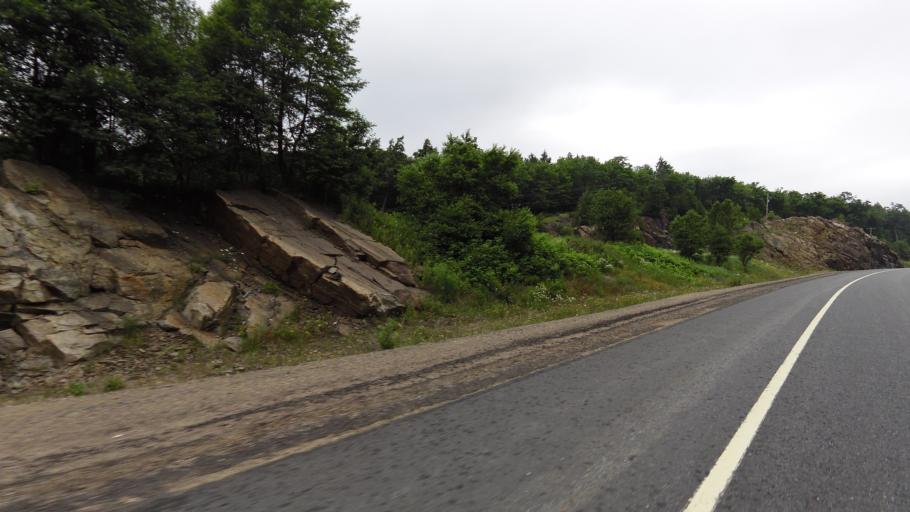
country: CA
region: Ontario
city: Huntsville
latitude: 45.5183
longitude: -78.7164
